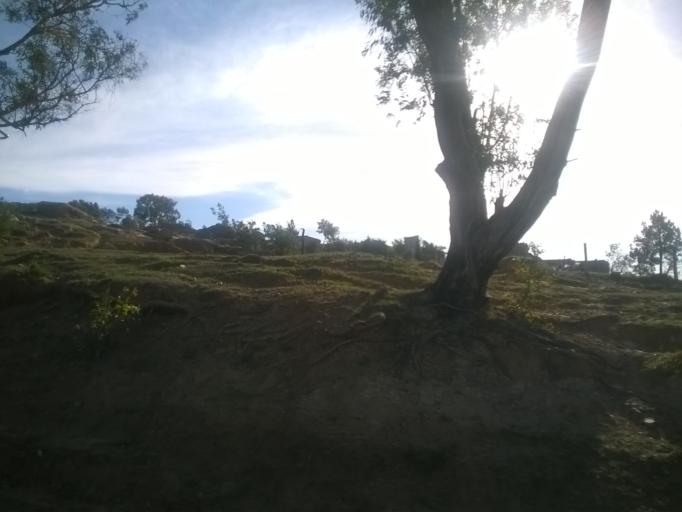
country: LS
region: Berea
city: Teyateyaneng
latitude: -29.1358
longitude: 27.7586
